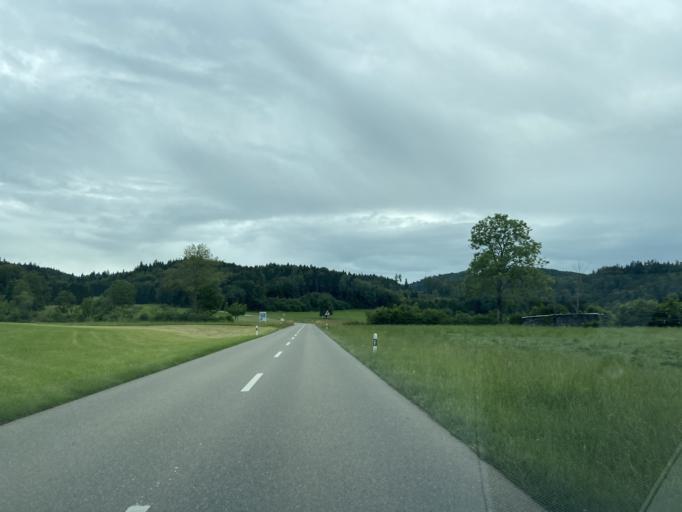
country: CH
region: Thurgau
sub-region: Muenchwilen District
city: Aadorf
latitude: 47.4731
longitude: 8.8939
